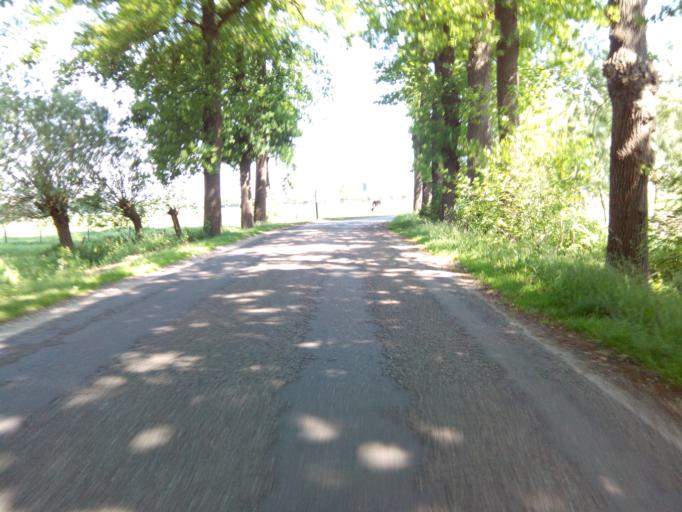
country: NL
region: Utrecht
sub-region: Gemeente Utrechtse Heuvelrug
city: Overberg
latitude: 52.0567
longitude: 5.4556
